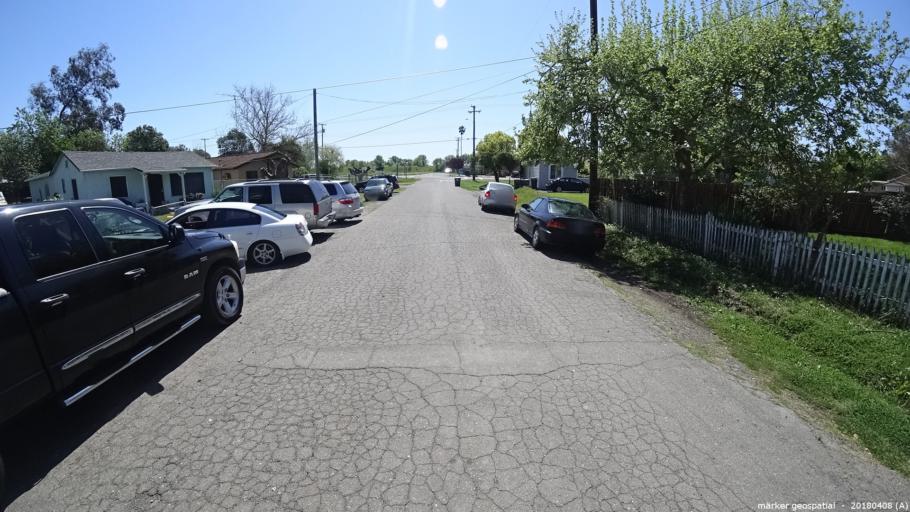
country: US
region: California
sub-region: Sacramento County
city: Laguna
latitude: 38.3682
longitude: -121.5159
